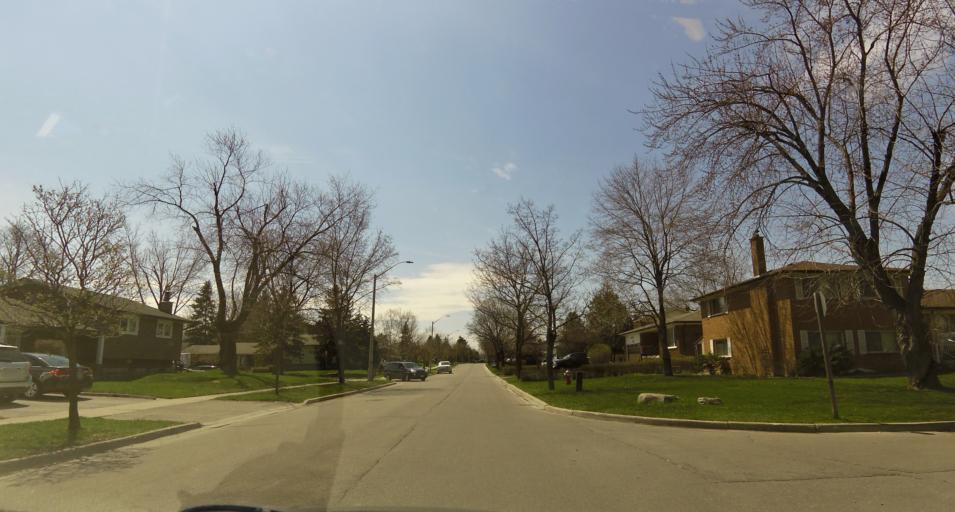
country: CA
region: Ontario
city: Mississauga
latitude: 43.6036
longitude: -79.7218
